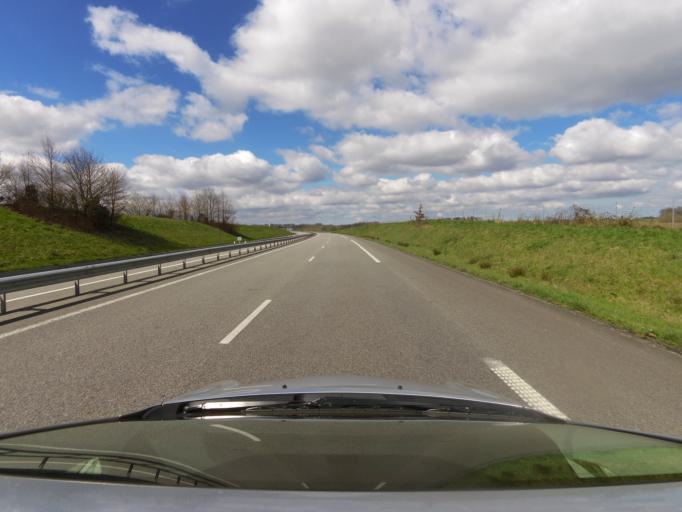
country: FR
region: Haute-Normandie
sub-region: Departement de la Seine-Maritime
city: Yerville
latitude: 49.6593
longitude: 0.9444
